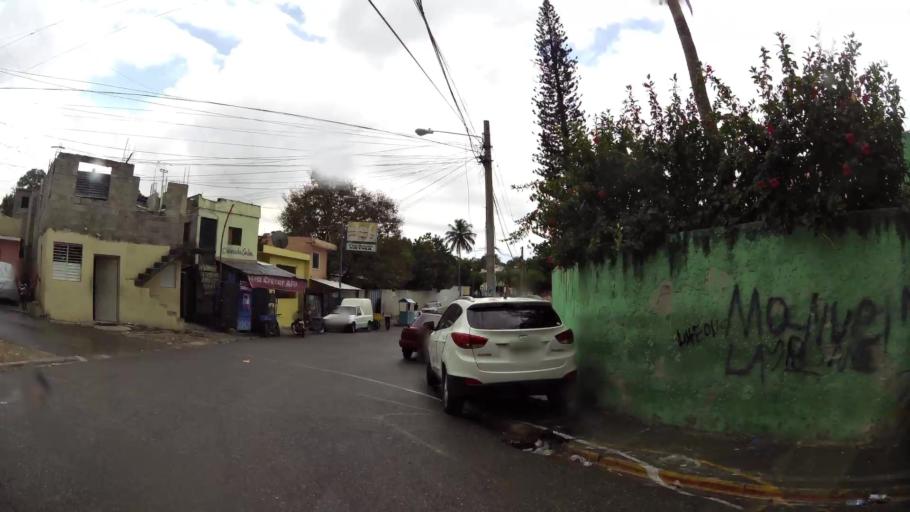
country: DO
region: Nacional
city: La Agustina
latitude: 18.5011
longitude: -69.9397
